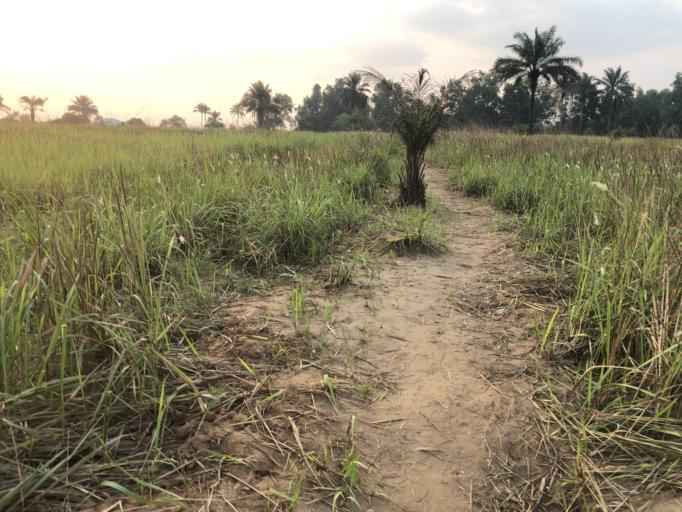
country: CD
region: Bandundu
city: Kikwit
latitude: -5.0737
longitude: 18.8488
